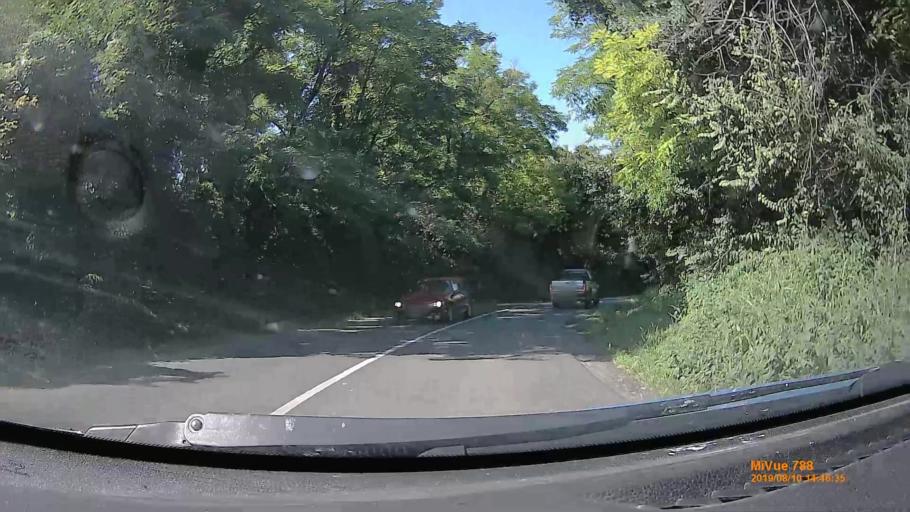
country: HU
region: Somogy
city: Somogyvar
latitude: 46.5922
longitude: 17.6434
